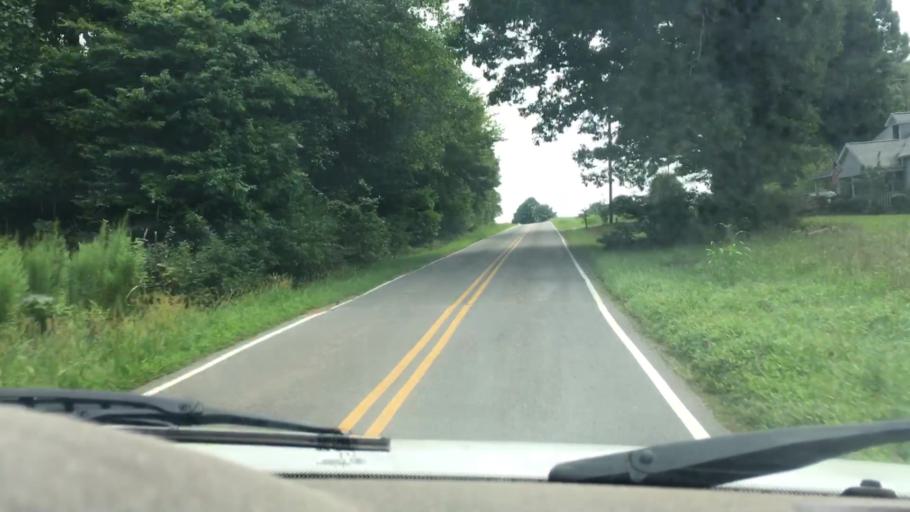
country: US
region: North Carolina
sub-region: Iredell County
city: Troutman
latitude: 35.6688
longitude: -80.8327
